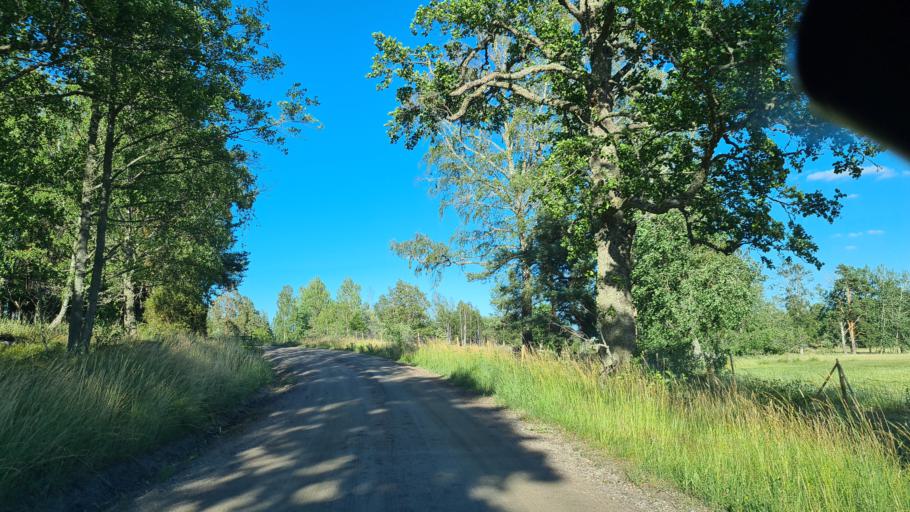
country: SE
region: Soedermanland
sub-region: Nykopings Kommun
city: Nykoping
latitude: 58.9072
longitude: 16.9651
